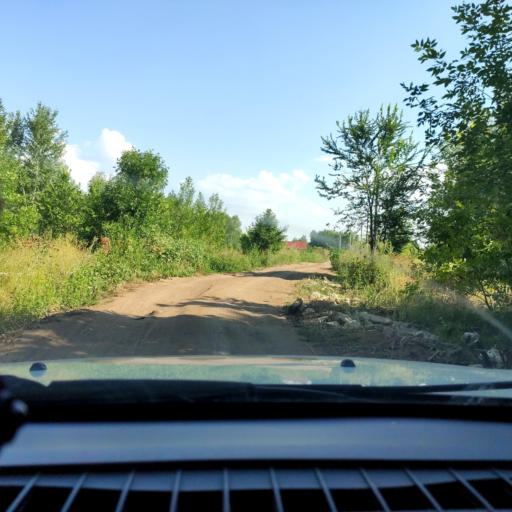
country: RU
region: Samara
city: Smyshlyayevka
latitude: 53.2045
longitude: 50.3303
